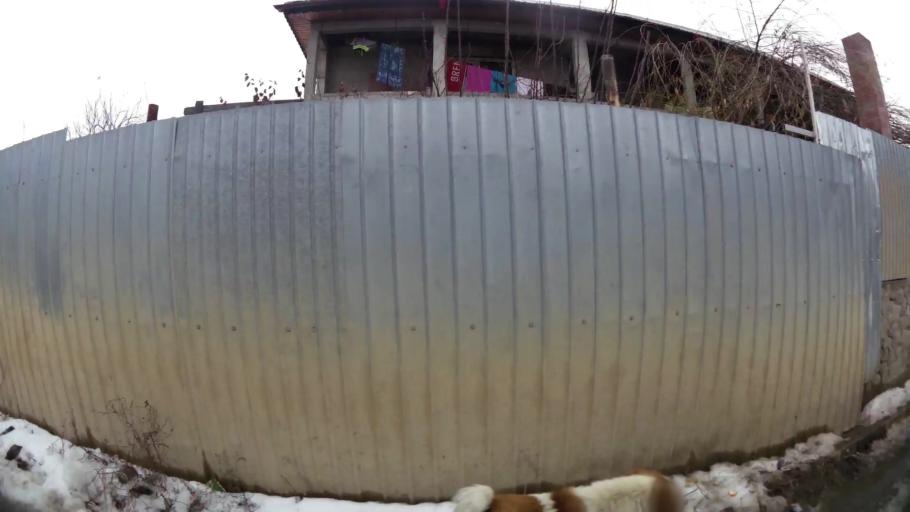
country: RO
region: Ilfov
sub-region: Comuna Pantelimon
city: Pantelimon
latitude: 44.4618
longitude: 26.2032
